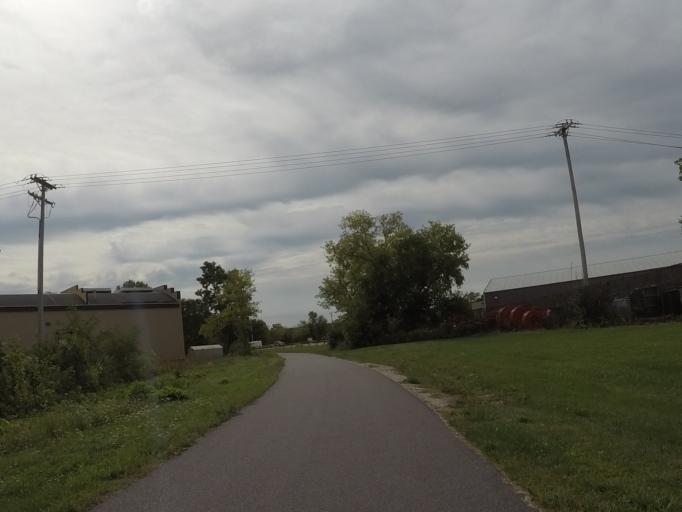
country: US
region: Wisconsin
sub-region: Sauk County
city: Sauk City
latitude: 43.2669
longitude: -89.7292
